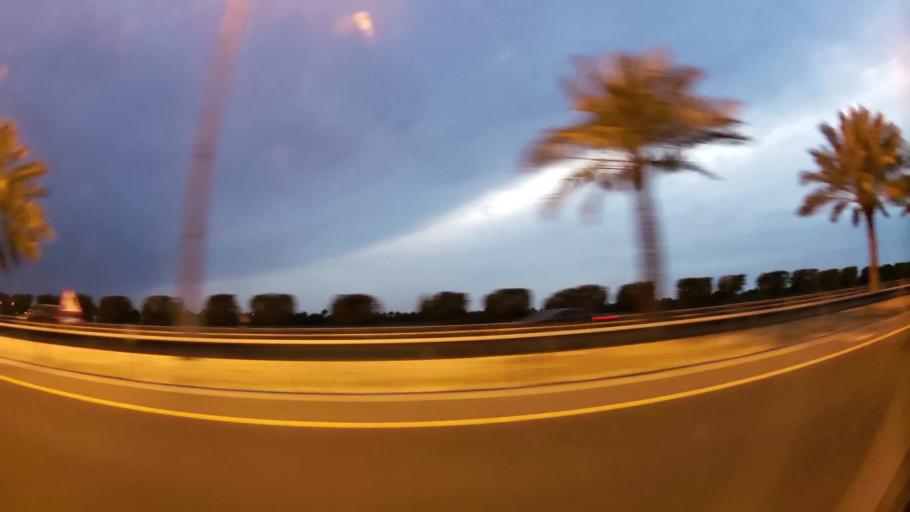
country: BH
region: Central Governorate
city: Madinat Hamad
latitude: 26.1554
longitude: 50.5066
